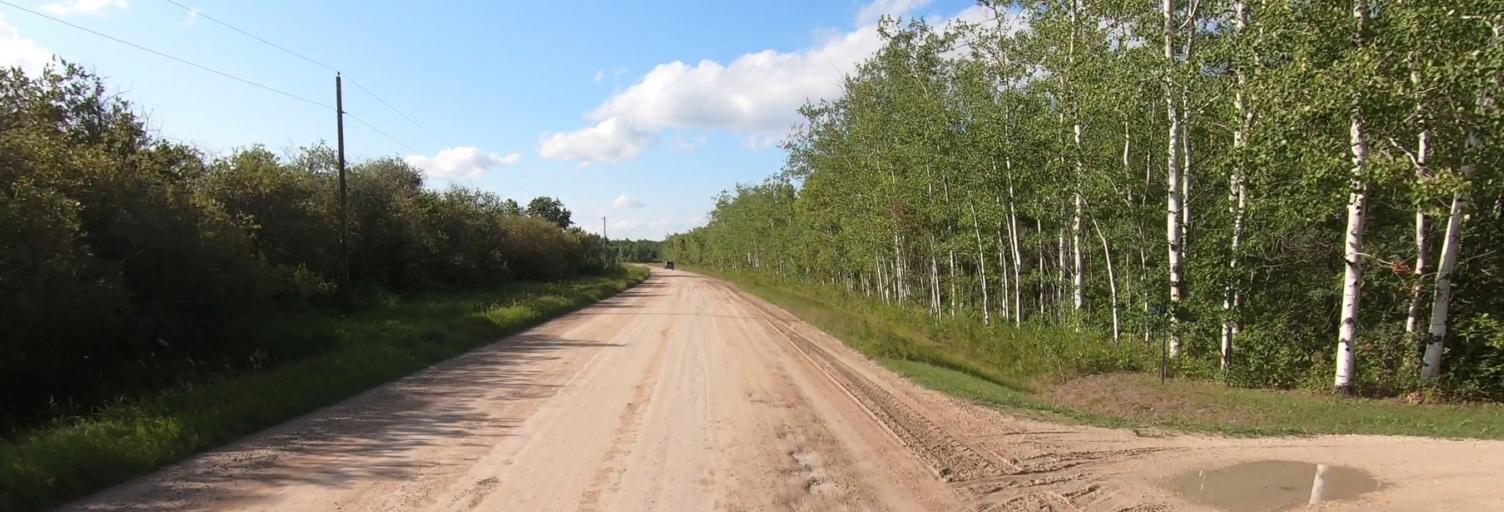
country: CA
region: Manitoba
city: Selkirk
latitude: 50.2328
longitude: -96.8410
